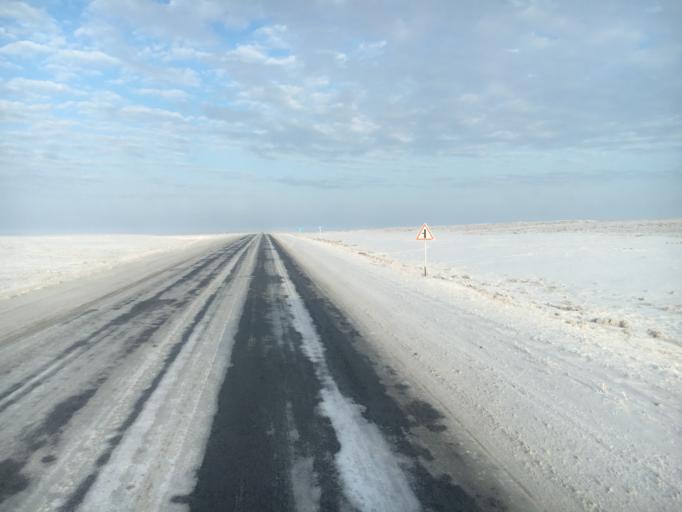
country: KZ
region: Qyzylorda
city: Sekseuil
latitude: 47.7155
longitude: 61.3981
